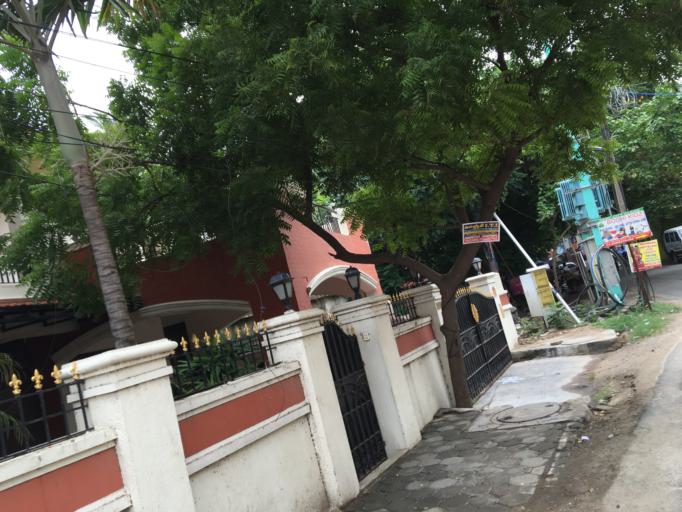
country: IN
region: Tamil Nadu
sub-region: Kancheepuram
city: Alandur
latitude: 12.9892
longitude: 80.2148
